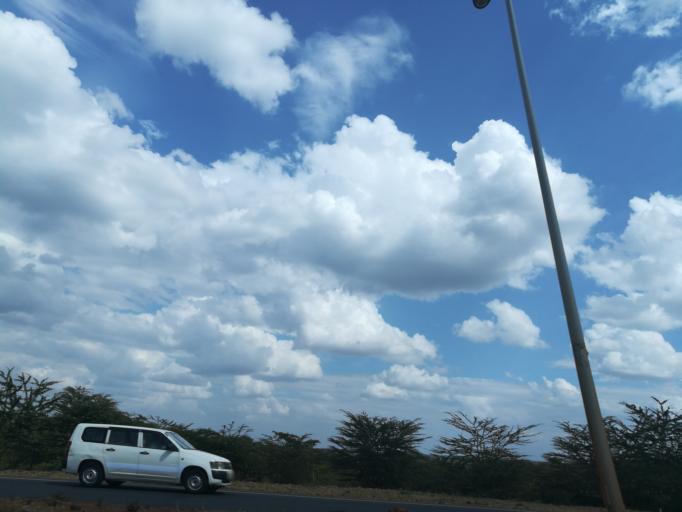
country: KE
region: Nairobi Area
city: Nairobi
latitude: -1.3328
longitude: 36.8065
